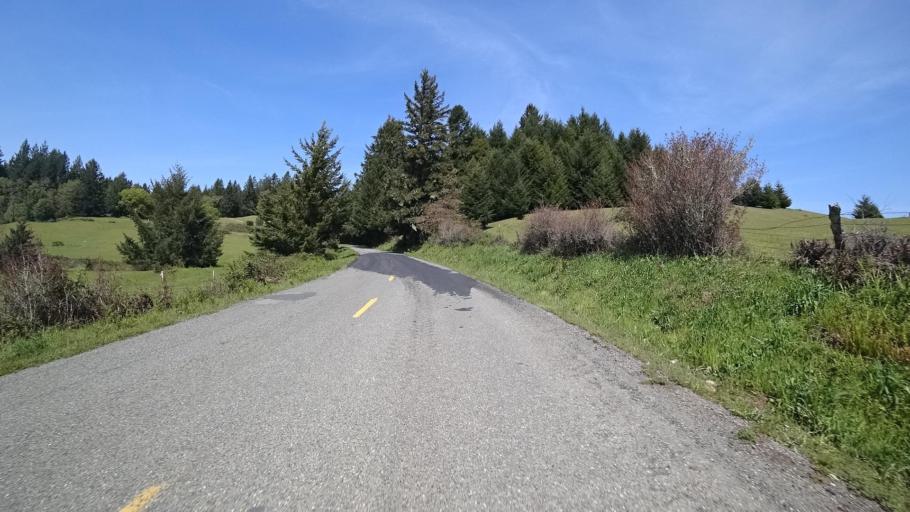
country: US
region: California
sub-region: Humboldt County
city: Redway
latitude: 40.3938
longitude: -123.7457
